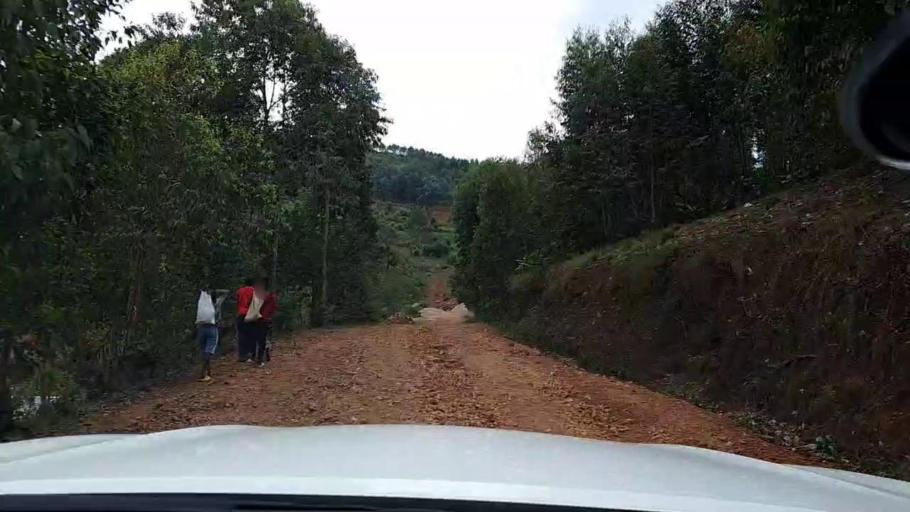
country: RW
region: Western Province
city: Kibuye
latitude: -2.1875
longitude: 29.2991
